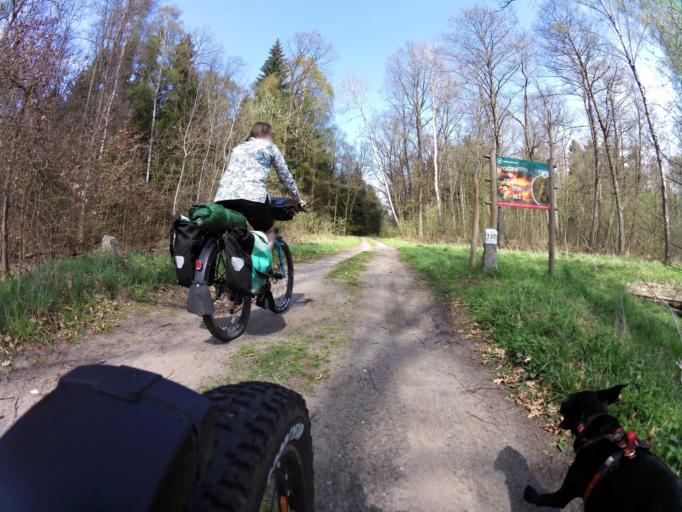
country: PL
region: West Pomeranian Voivodeship
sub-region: Powiat lobeski
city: Resko
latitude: 53.8066
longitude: 15.4453
